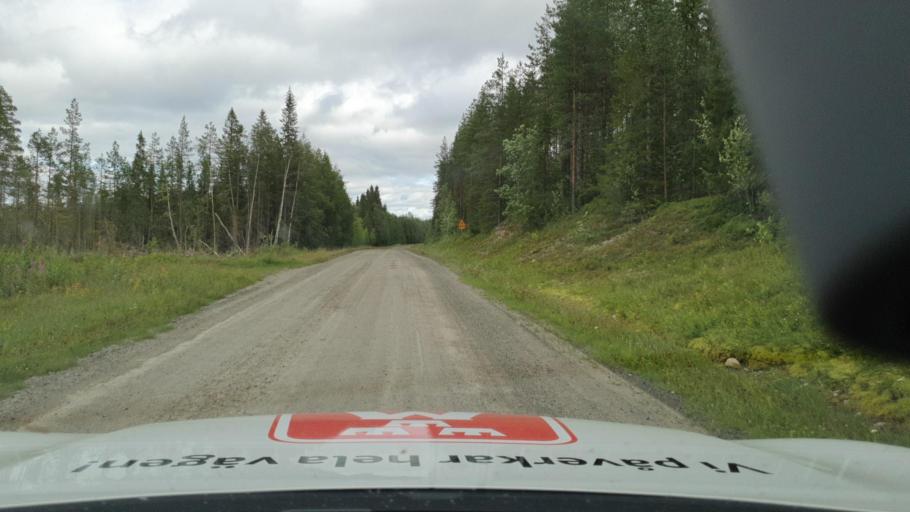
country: SE
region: Vaesterbotten
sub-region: Dorotea Kommun
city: Dorotea
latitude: 64.2076
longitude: 16.8042
